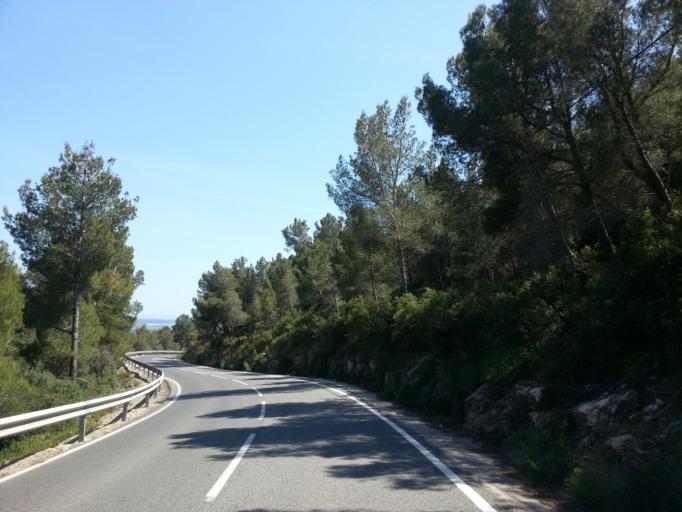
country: ES
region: Catalonia
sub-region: Provincia de Tarragona
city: Alcover
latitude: 41.2728
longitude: 1.1708
